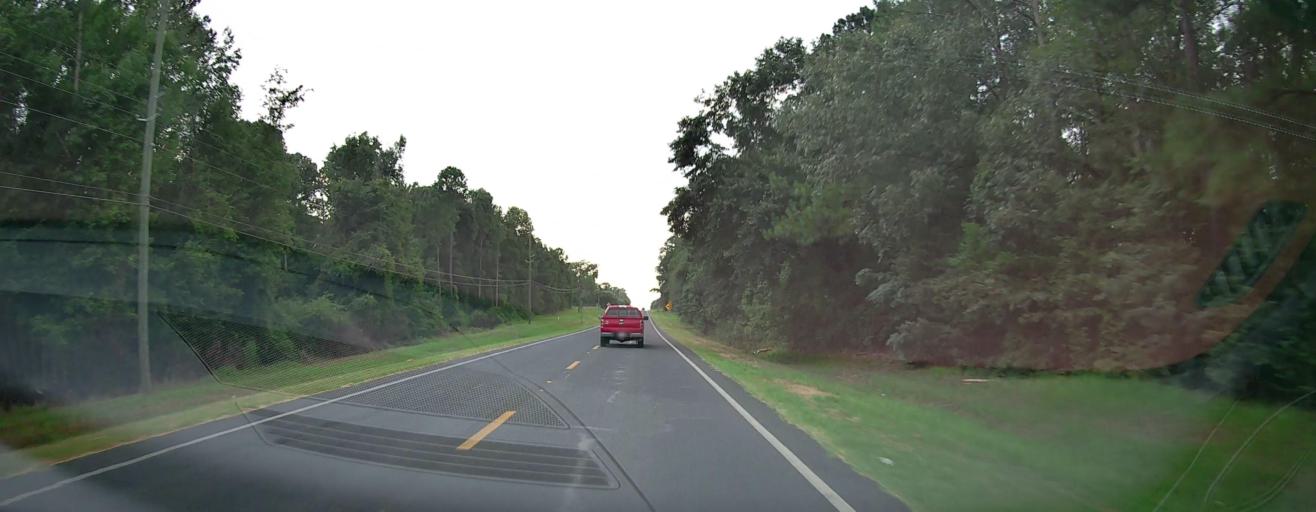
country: US
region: Georgia
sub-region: Laurens County
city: East Dublin
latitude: 32.5351
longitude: -82.8423
